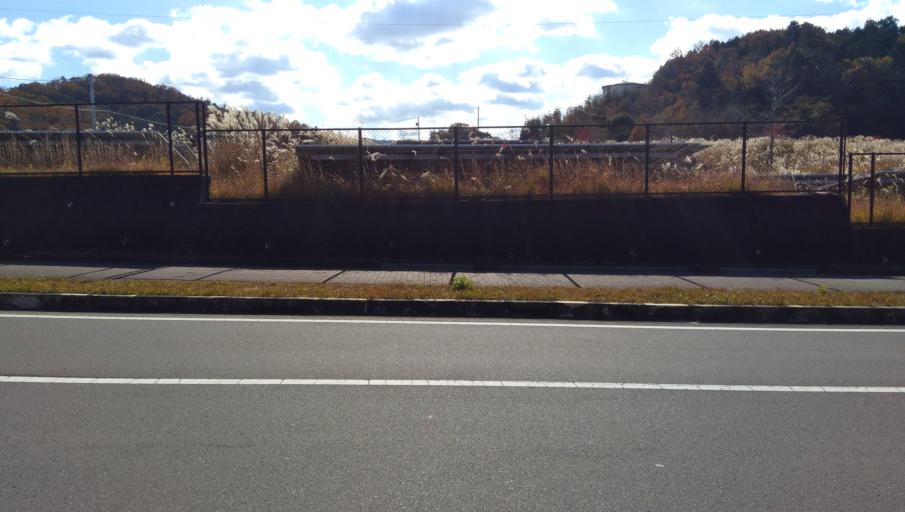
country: JP
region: Mie
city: Nabari
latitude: 34.6129
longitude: 136.1213
